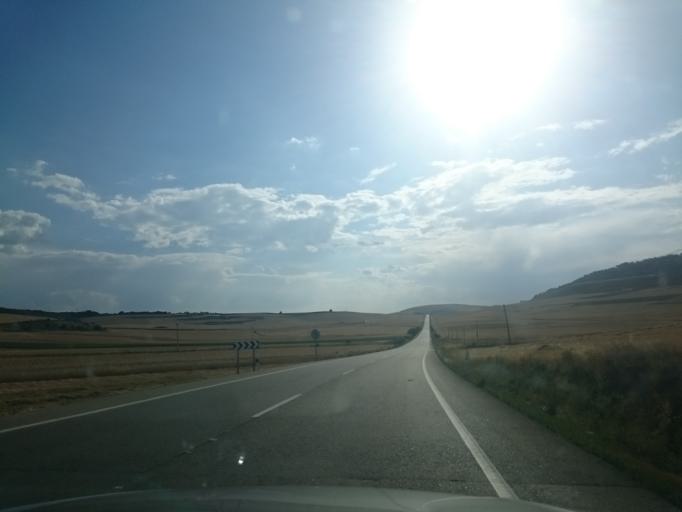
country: ES
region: Castille and Leon
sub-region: Provincia de Burgos
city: Viloria de Rioja
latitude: 42.4324
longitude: -3.1008
